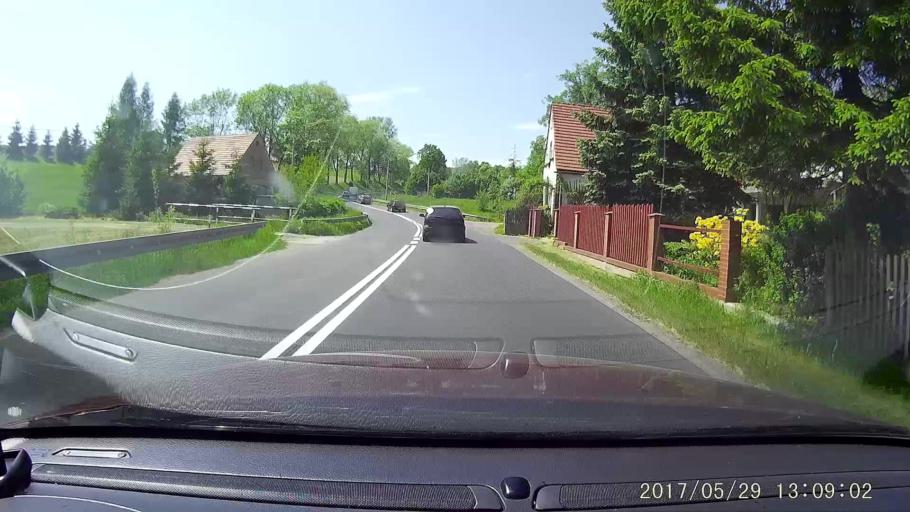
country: PL
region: Lower Silesian Voivodeship
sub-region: Powiat jeleniogorski
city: Stara Kamienica
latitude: 50.9626
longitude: 15.5525
